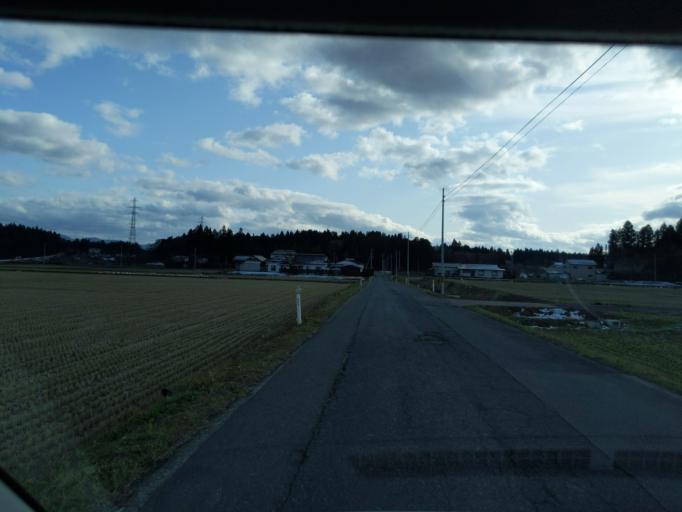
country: JP
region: Iwate
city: Mizusawa
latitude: 39.1196
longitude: 141.0821
